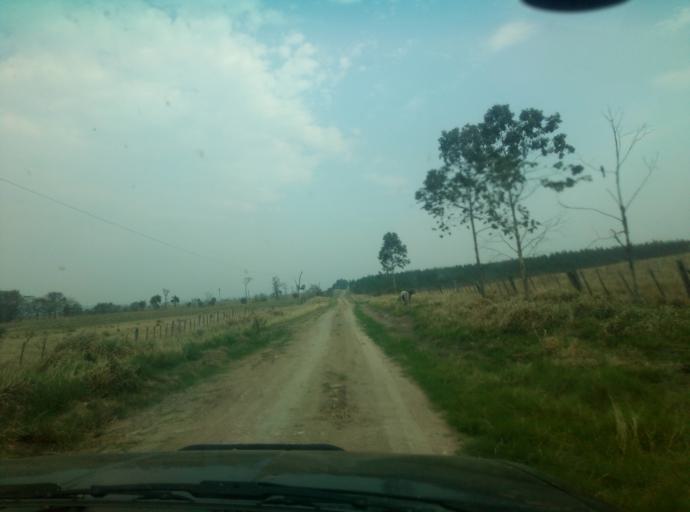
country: PY
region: Caaguazu
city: San Joaquin
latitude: -25.1063
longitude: -56.1276
